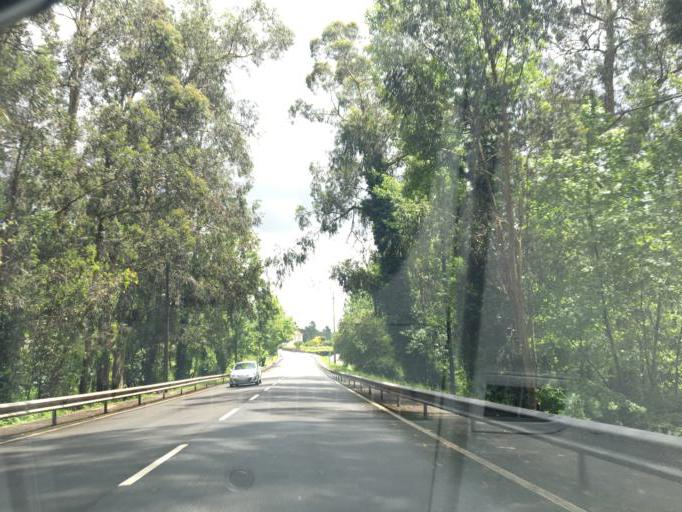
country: PT
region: Porto
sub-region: Maia
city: Anta
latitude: 41.2596
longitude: -8.6060
